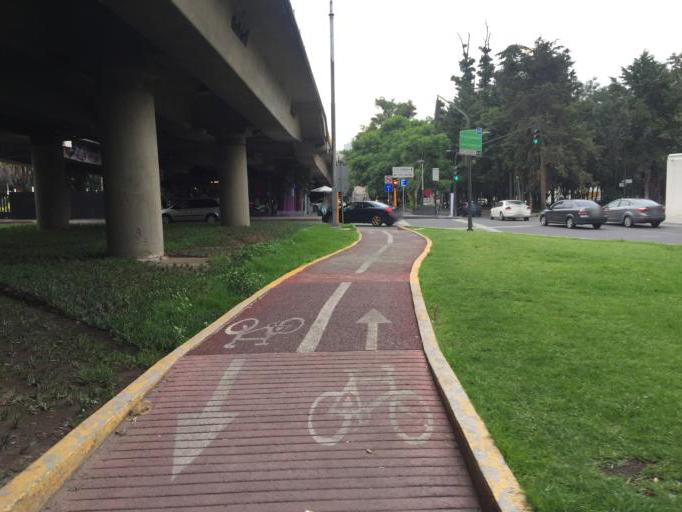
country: MX
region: Mexico City
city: Miguel Hidalgo
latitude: 19.4326
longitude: -99.2085
